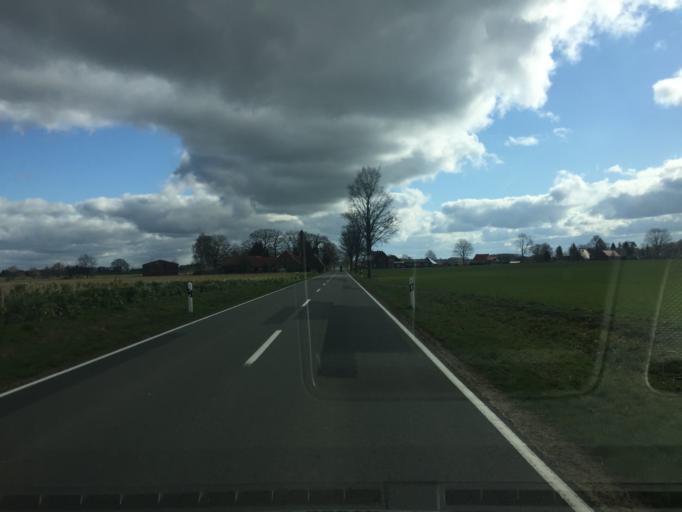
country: DE
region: Lower Saxony
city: Engeln
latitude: 52.7978
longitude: 8.9123
